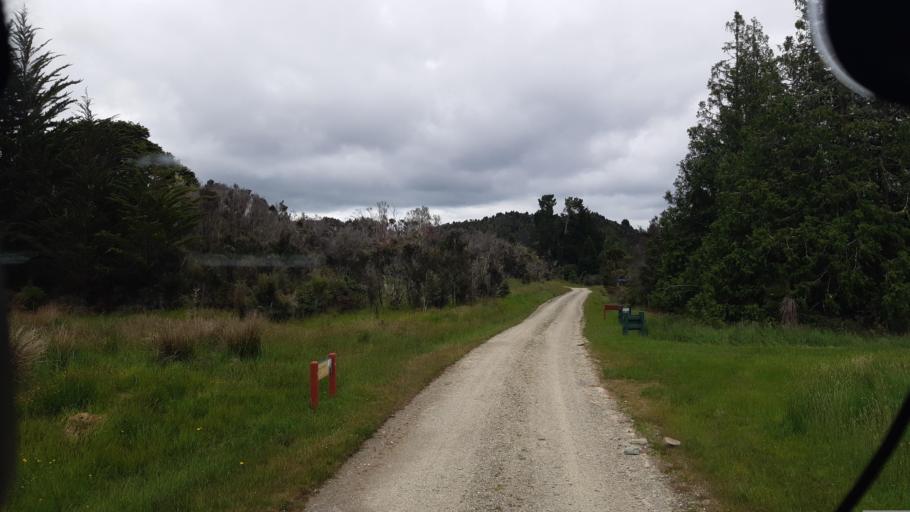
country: NZ
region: West Coast
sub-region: Buller District
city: Westport
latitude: -42.2950
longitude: 171.8213
